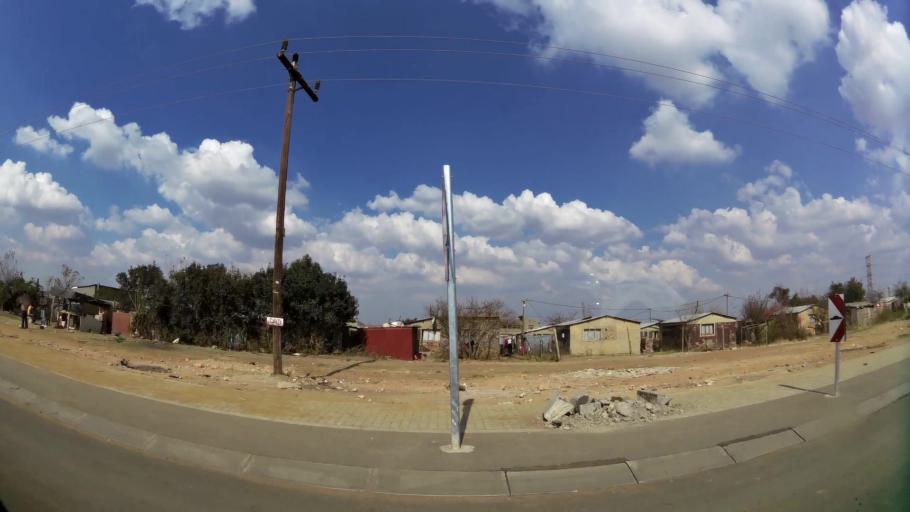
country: ZA
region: Gauteng
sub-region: City of Johannesburg Metropolitan Municipality
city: Roodepoort
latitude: -26.1941
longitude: 27.8716
